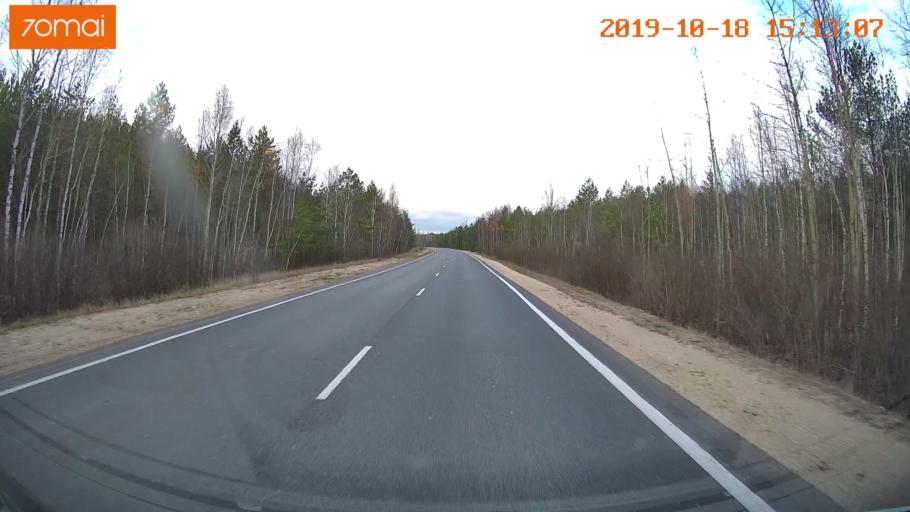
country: RU
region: Vladimir
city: Gus'-Khrustal'nyy
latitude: 55.5826
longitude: 40.7125
